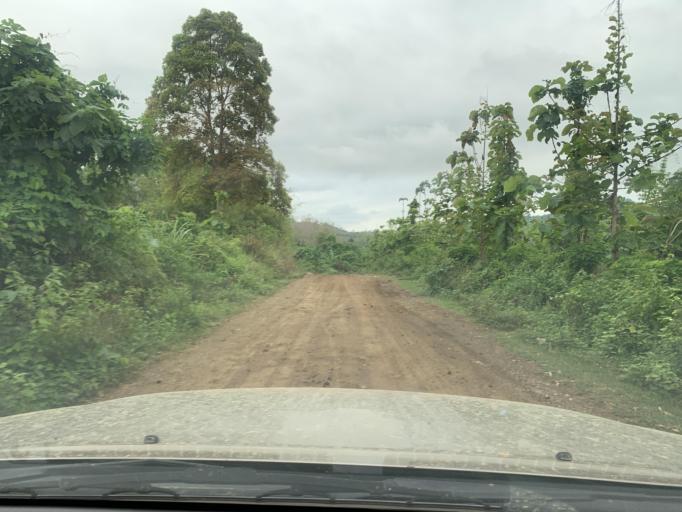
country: TH
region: Uttaradit
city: Ban Khok
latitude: 18.4006
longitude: 101.4315
